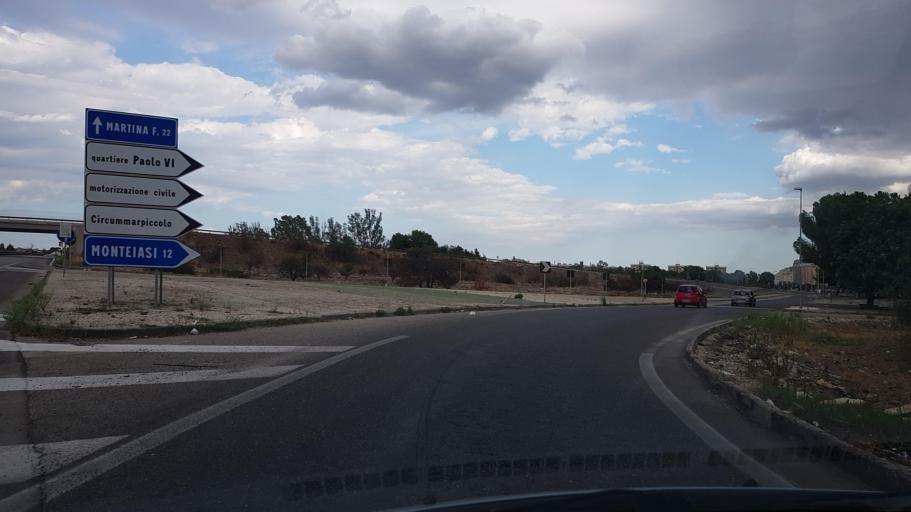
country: IT
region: Apulia
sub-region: Provincia di Taranto
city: Paolo VI
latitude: 40.5201
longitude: 17.2598
